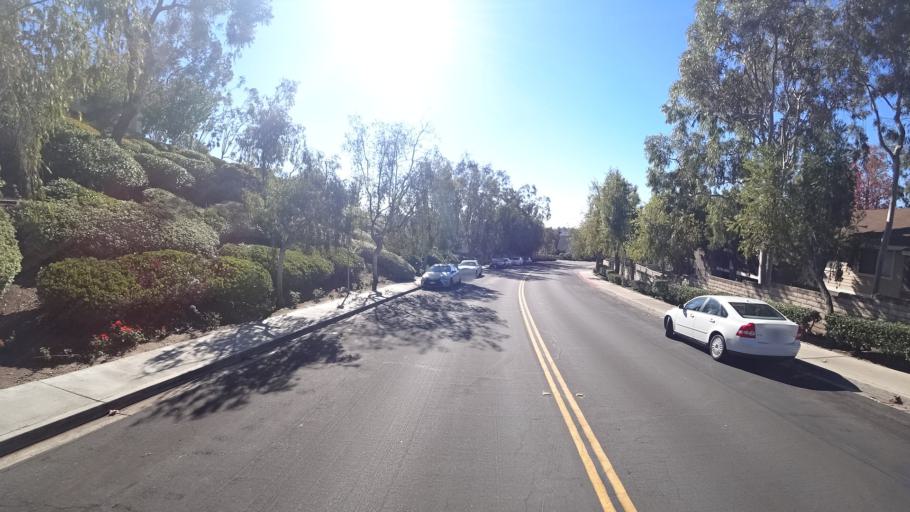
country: US
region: California
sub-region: Orange County
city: Lake Forest
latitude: 33.6546
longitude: -117.6847
